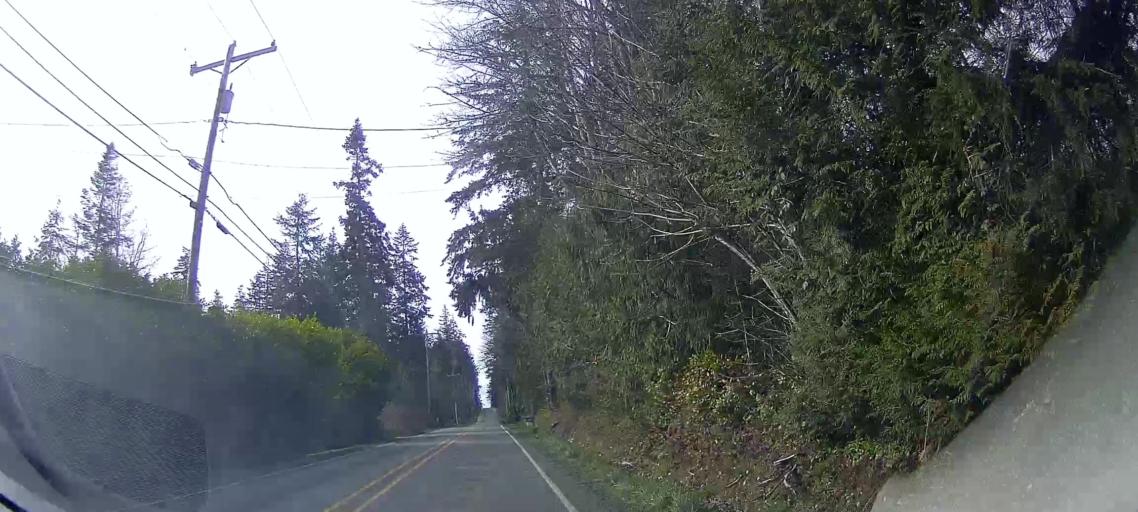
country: US
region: Washington
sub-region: Island County
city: Camano
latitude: 48.1384
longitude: -122.4832
